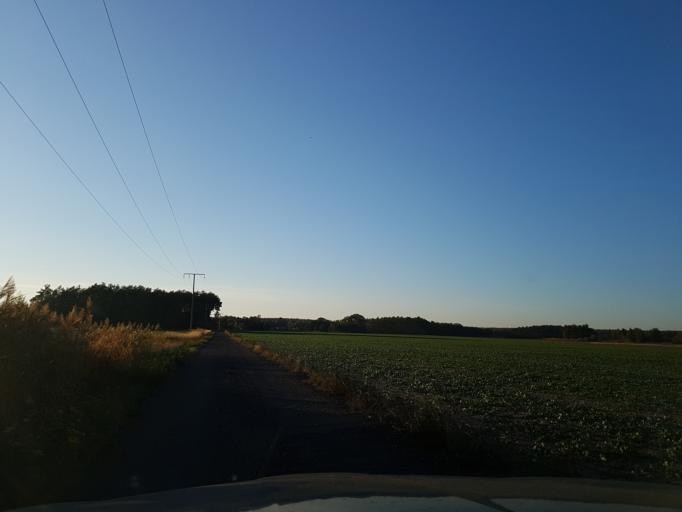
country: DE
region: Brandenburg
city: Bad Liebenwerda
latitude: 51.5468
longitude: 13.3921
